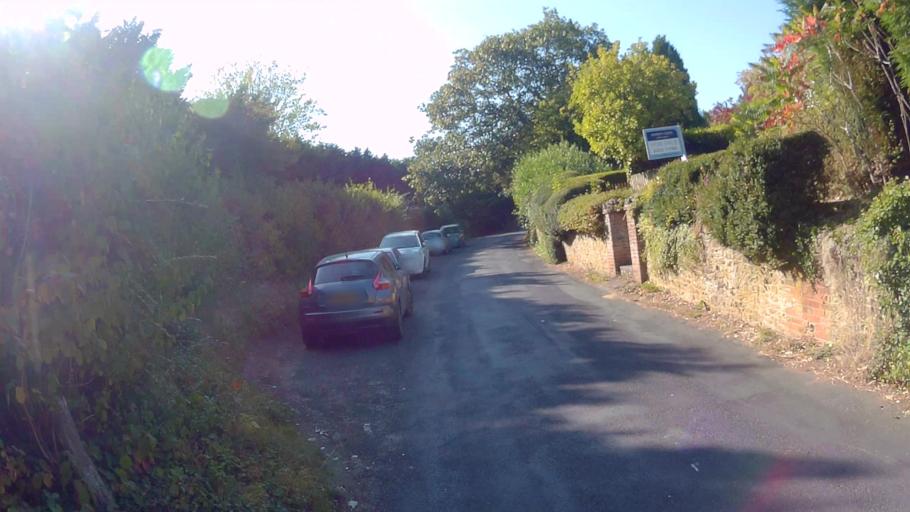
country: GB
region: England
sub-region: Surrey
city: Churt
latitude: 51.1731
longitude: -0.7886
